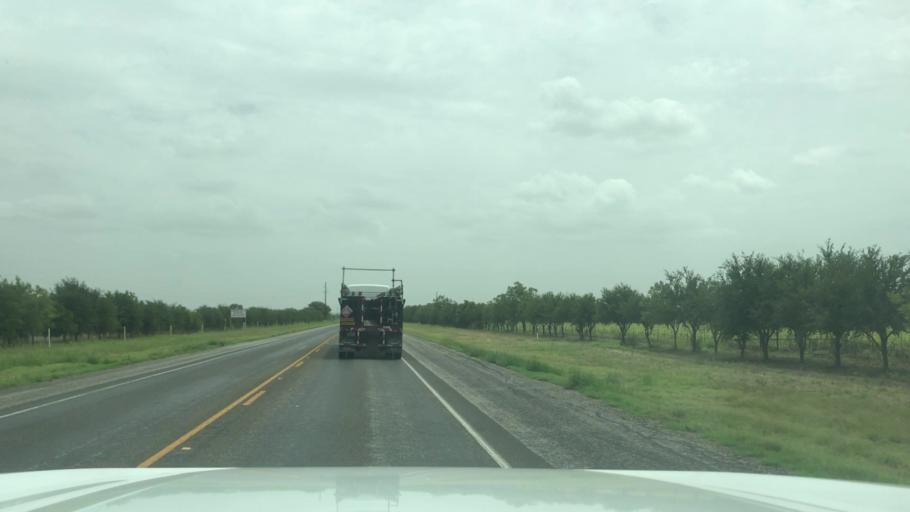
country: US
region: Texas
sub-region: Bosque County
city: Clifton
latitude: 31.8012
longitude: -97.5994
